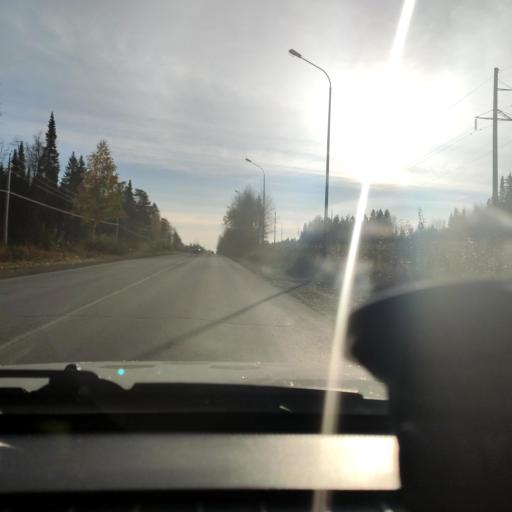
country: RU
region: Perm
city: Ferma
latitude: 57.9496
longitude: 56.3957
